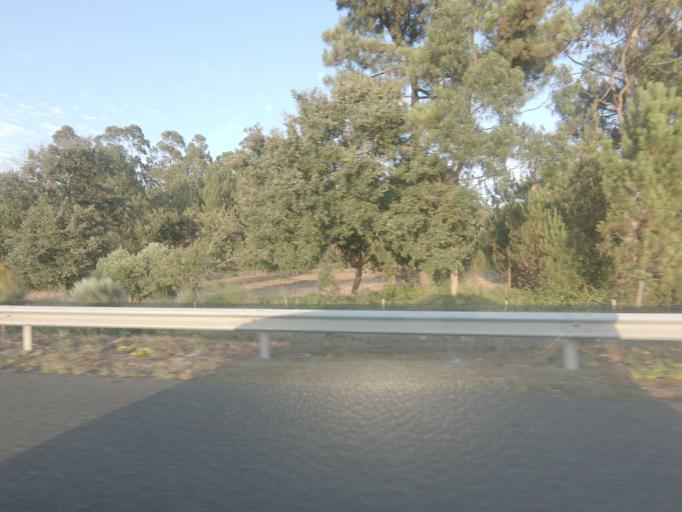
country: PT
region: Leiria
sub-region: Leiria
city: Santa Catarina da Serra
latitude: 39.6335
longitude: -8.6986
